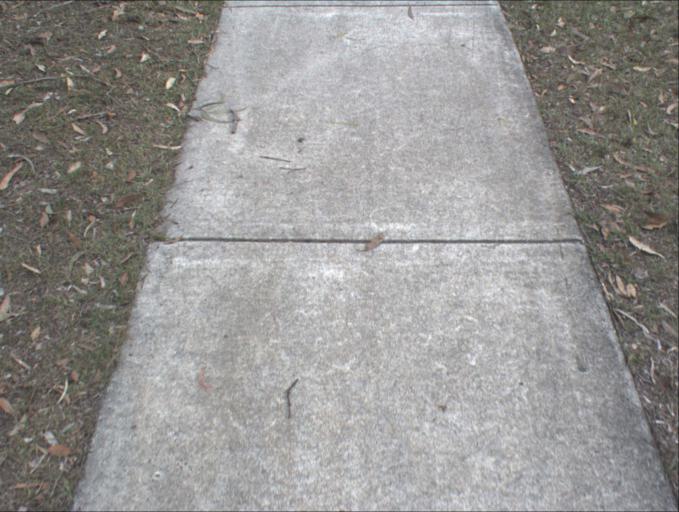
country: AU
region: Queensland
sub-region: Logan
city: Logan Reserve
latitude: -27.7227
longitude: 153.0902
